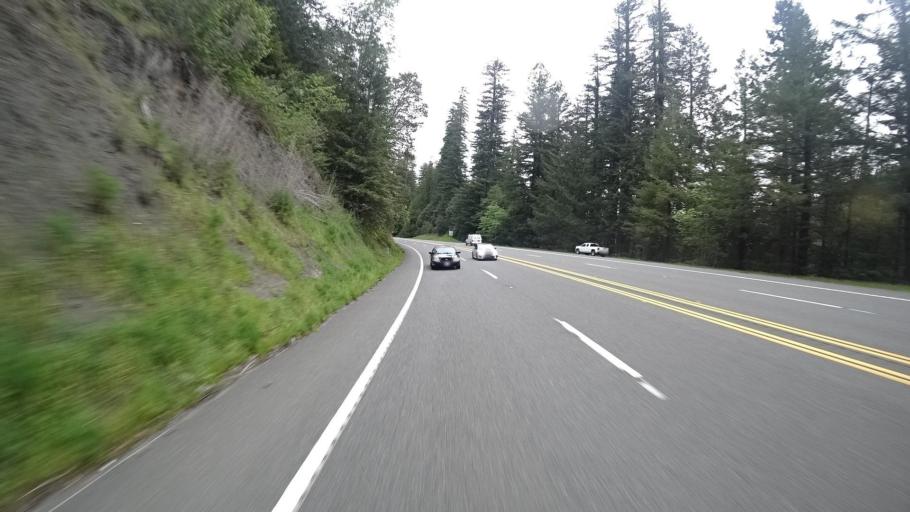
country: US
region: California
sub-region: Humboldt County
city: Rio Dell
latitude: 40.3623
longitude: -123.9200
